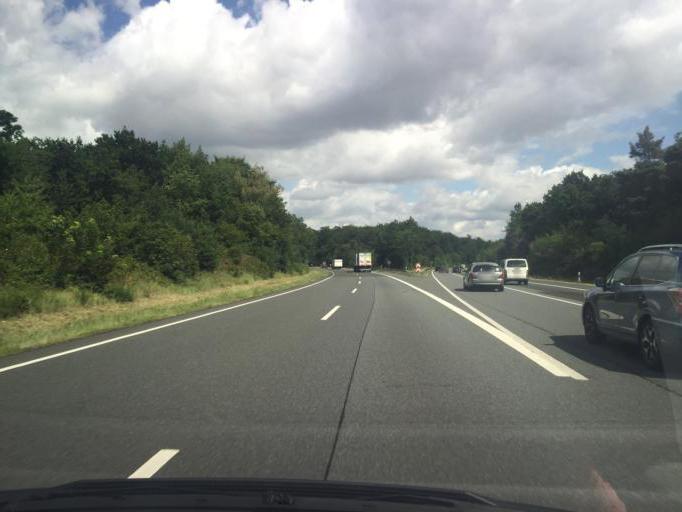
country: DE
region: Hesse
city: Raunheim
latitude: 50.0216
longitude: 8.4969
